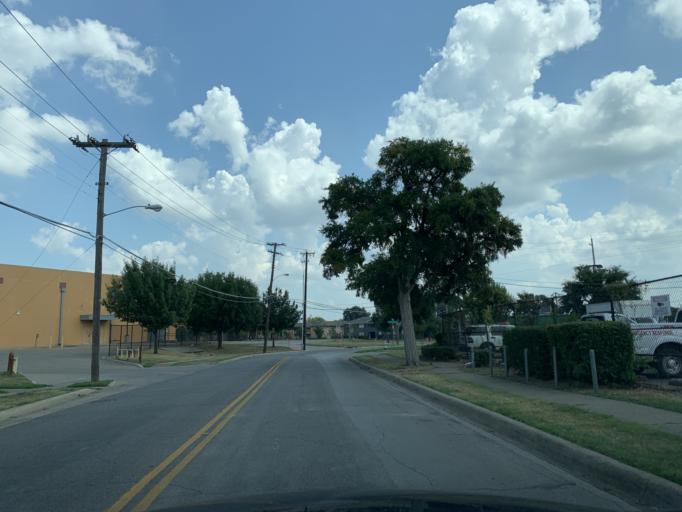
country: US
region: Texas
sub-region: Dallas County
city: Dallas
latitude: 32.7446
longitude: -96.8171
